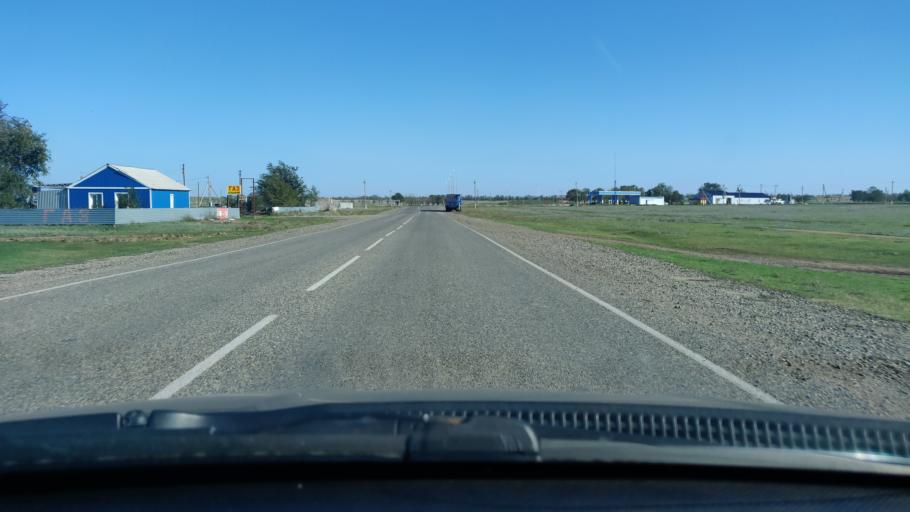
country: RU
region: Stavropol'skiy
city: Letnyaya Stavka
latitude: 45.3737
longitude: 43.6889
